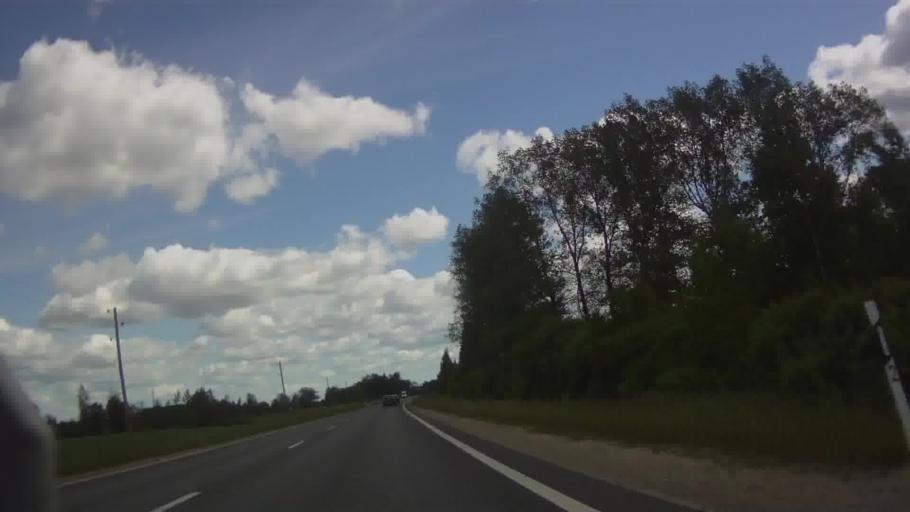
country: LV
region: Livani
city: Livani
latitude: 56.5308
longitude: 26.2273
